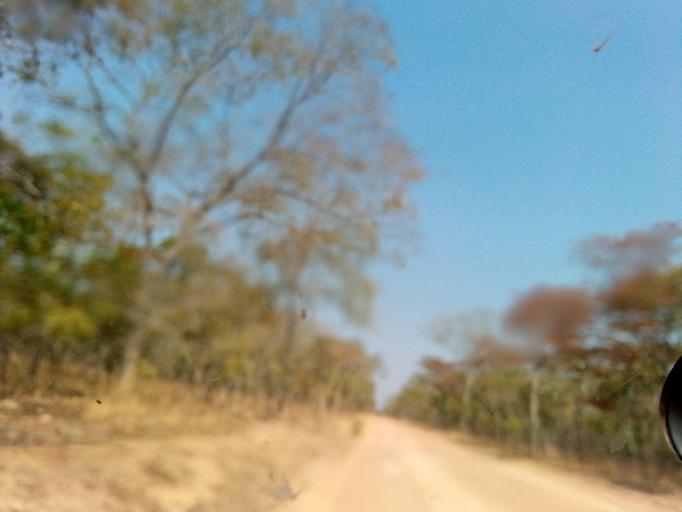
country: ZM
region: Northern
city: Mpika
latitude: -12.2420
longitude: 30.8318
